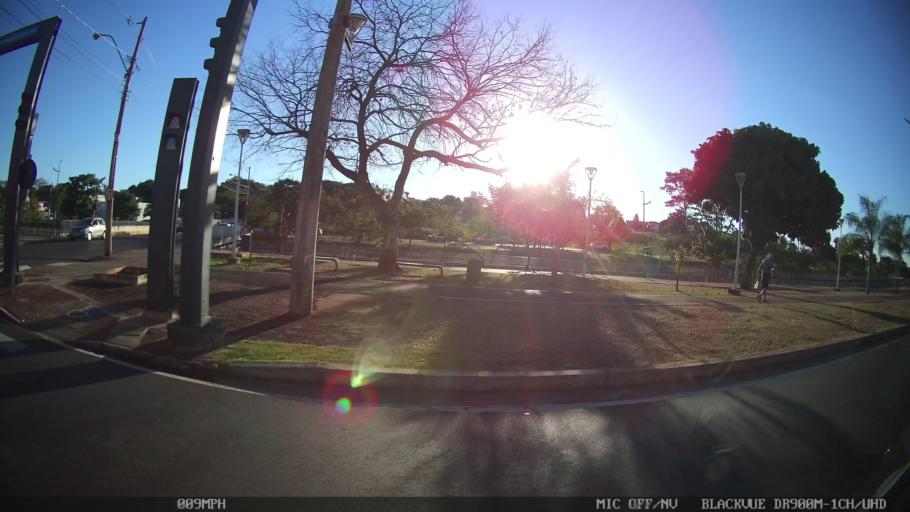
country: BR
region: Sao Paulo
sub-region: Sao Jose Do Rio Preto
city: Sao Jose do Rio Preto
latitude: -20.7959
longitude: -49.3762
